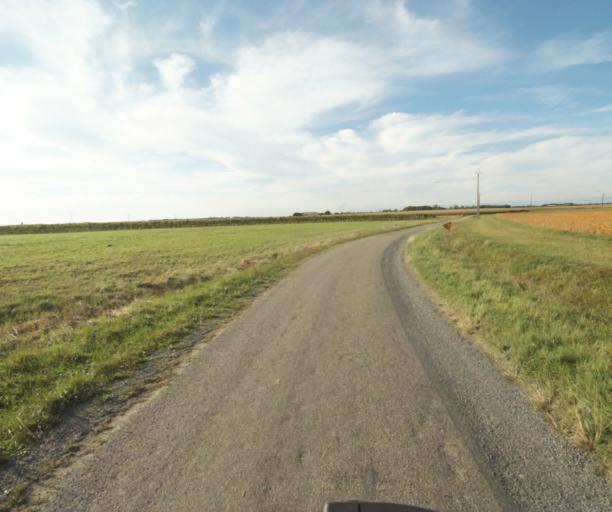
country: FR
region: Midi-Pyrenees
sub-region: Departement du Tarn-et-Garonne
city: Finhan
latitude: 43.9052
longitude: 1.1306
